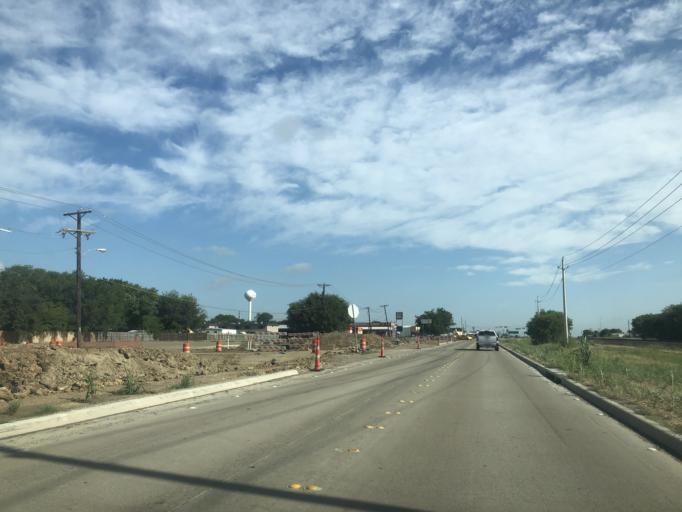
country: US
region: Texas
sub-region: Denton County
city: Justin
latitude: 33.0814
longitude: -97.2958
